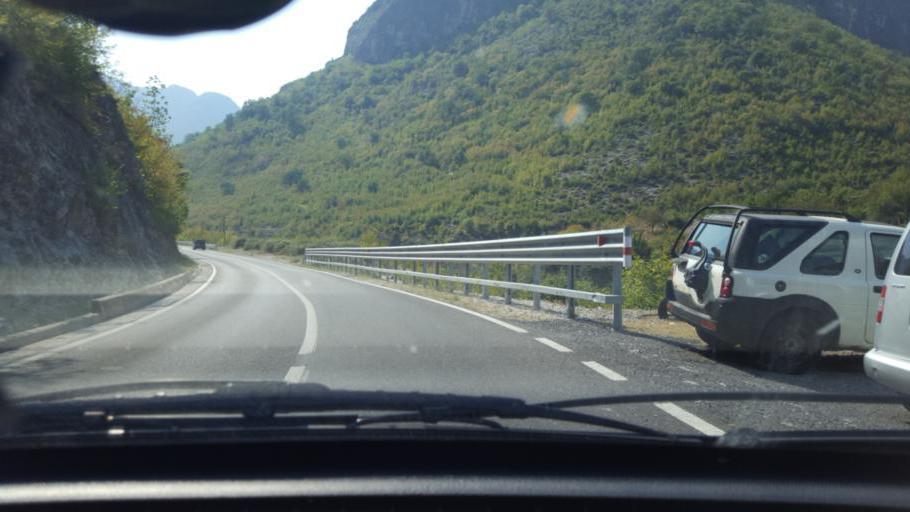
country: AL
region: Shkoder
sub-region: Rrethi i Malesia e Madhe
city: Kastrat
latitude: 42.4428
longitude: 19.5400
